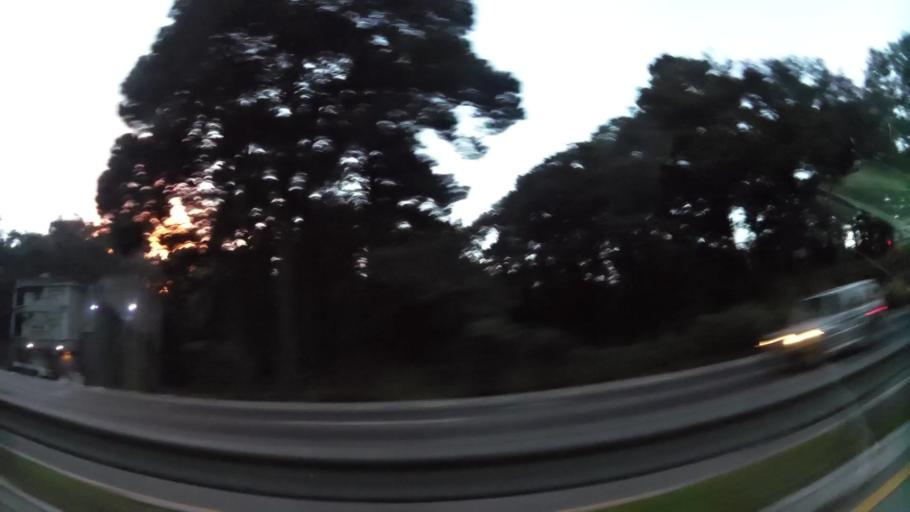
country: GT
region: Guatemala
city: Mixco
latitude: 14.6184
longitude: -90.6171
